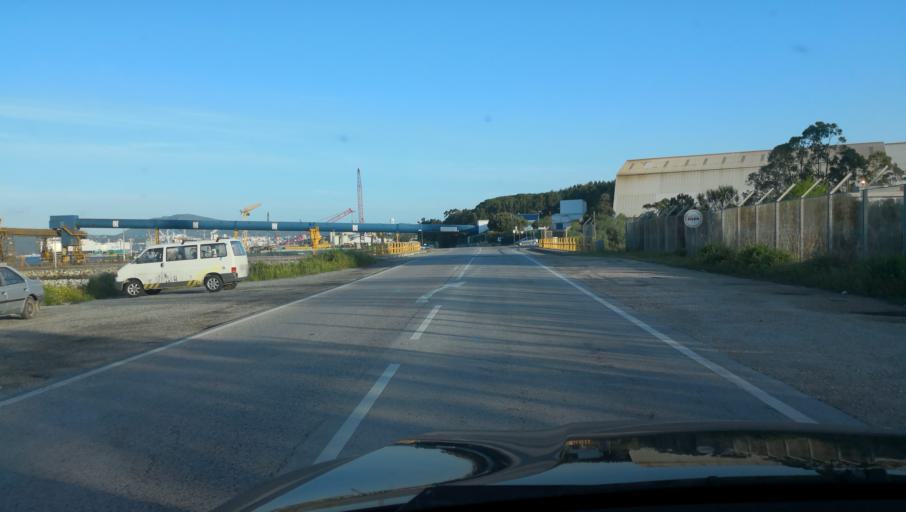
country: PT
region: Setubal
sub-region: Setubal
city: Setubal
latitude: 38.5073
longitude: -8.8487
